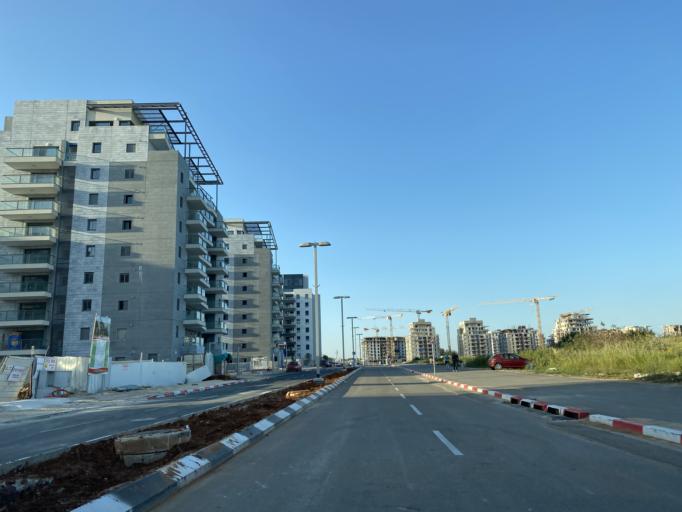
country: IL
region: Tel Aviv
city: Herzliyya
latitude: 32.1573
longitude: 34.8226
